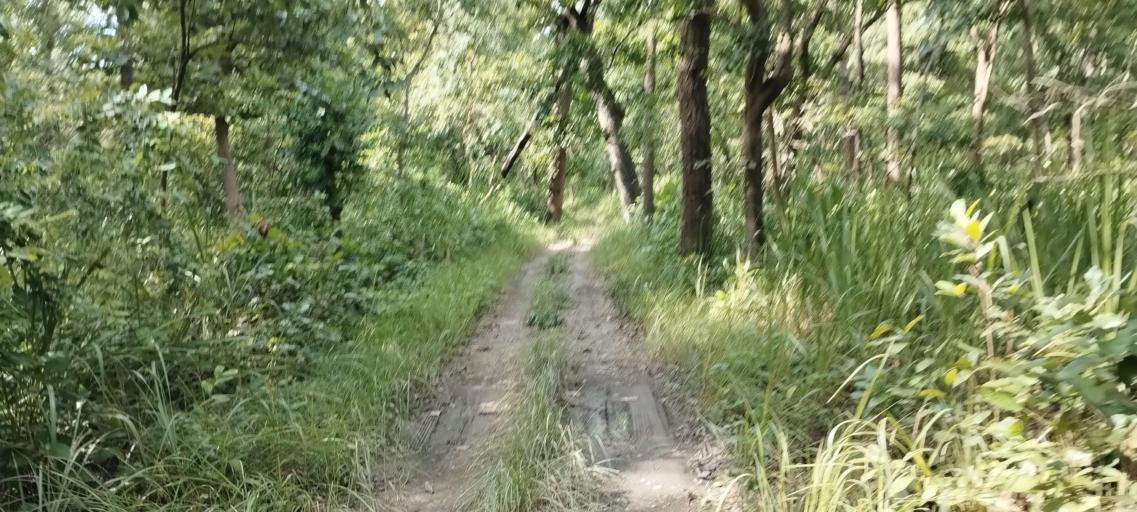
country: NP
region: Far Western
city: Tikapur
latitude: 28.5637
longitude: 81.2939
